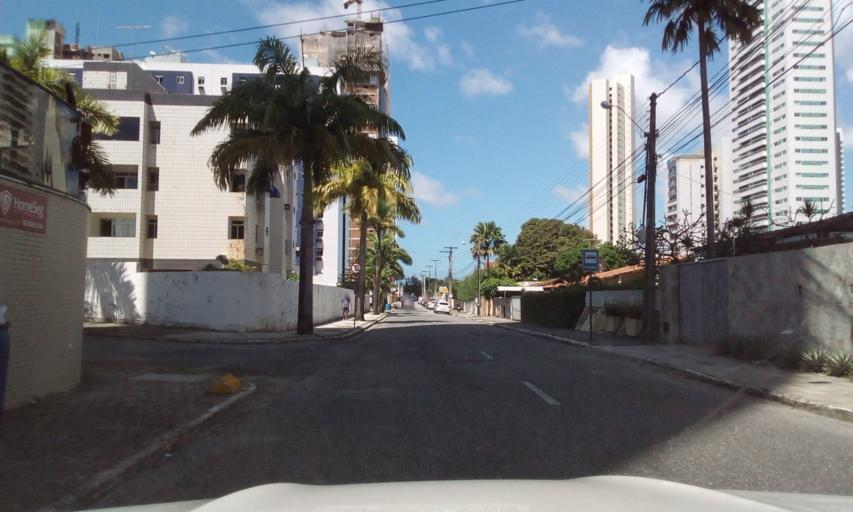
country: BR
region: Paraiba
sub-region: Joao Pessoa
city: Joao Pessoa
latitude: -7.1136
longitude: -34.8401
